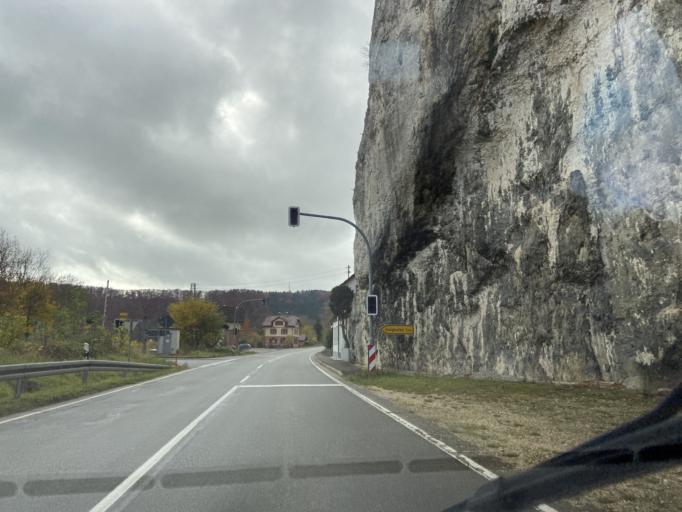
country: DE
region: Baden-Wuerttemberg
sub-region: Tuebingen Region
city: Inzigkofen
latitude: 48.0798
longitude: 9.1660
